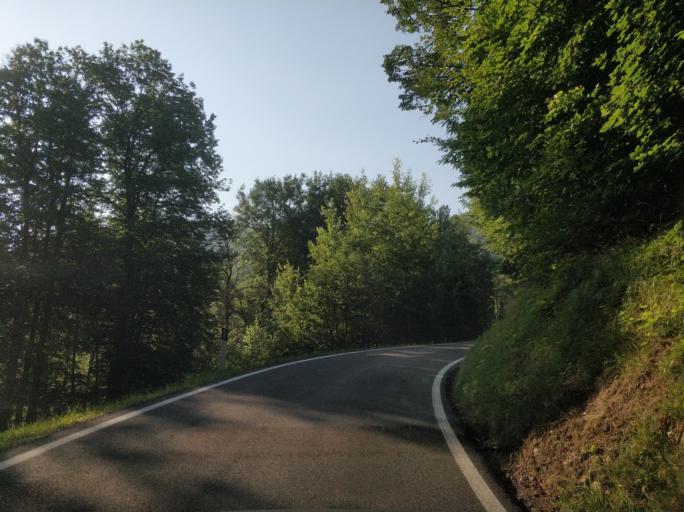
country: IT
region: Piedmont
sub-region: Provincia di Torino
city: Viu
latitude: 45.2271
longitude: 7.3772
